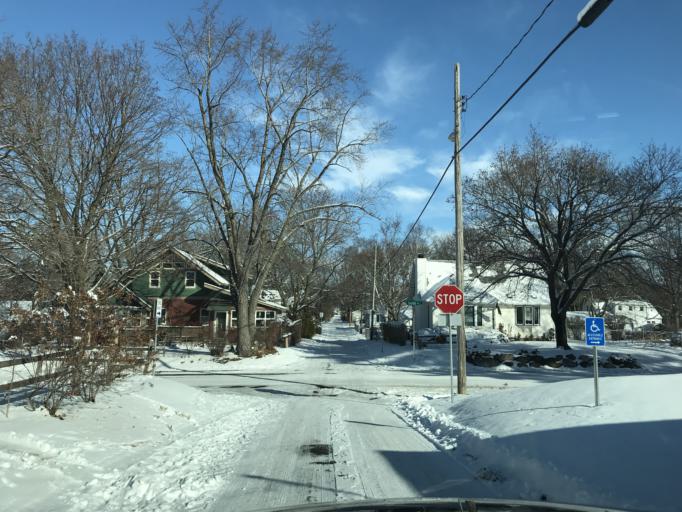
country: US
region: Wisconsin
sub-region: Dane County
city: Monona
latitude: 43.0787
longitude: -89.3209
